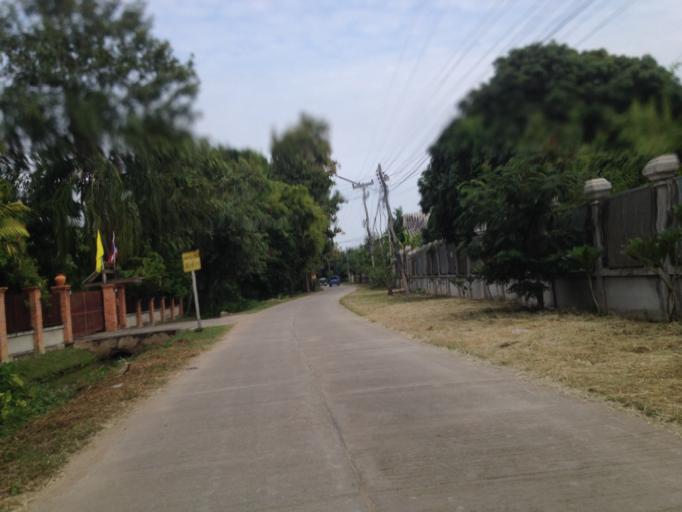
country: TH
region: Chiang Mai
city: San Pa Tong
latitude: 18.6649
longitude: 98.8869
